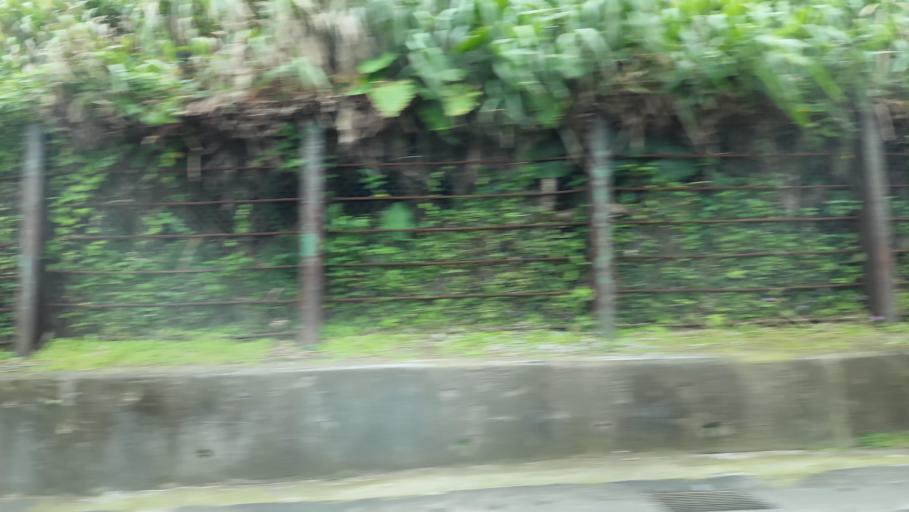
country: TW
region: Taiwan
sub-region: Keelung
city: Keelung
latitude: 25.1631
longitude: 121.7276
